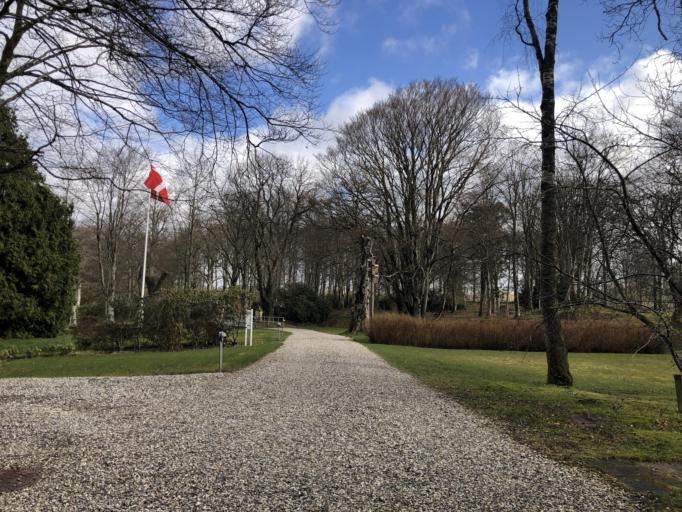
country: DK
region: Central Jutland
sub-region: Herning Kommune
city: Kibaek
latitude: 55.9491
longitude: 8.8816
